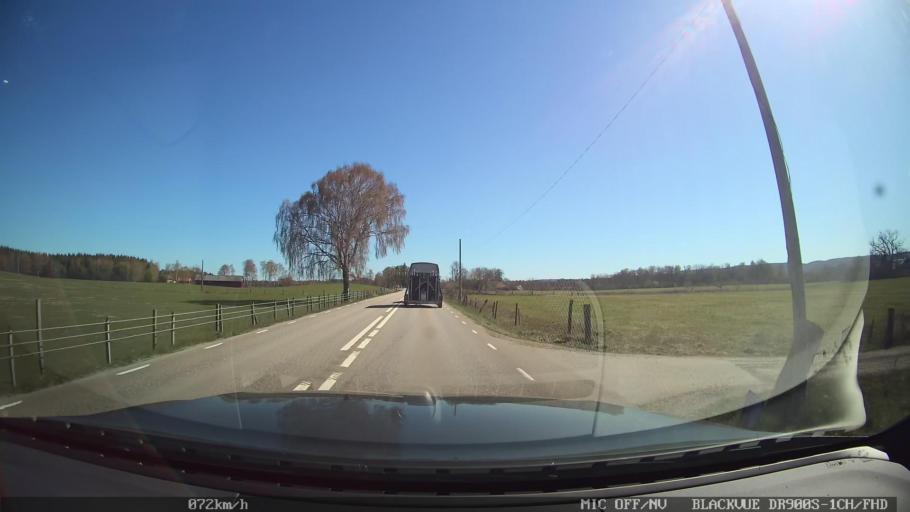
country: SE
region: Skane
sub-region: Klippans Kommun
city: Ljungbyhed
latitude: 56.0979
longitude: 13.1828
